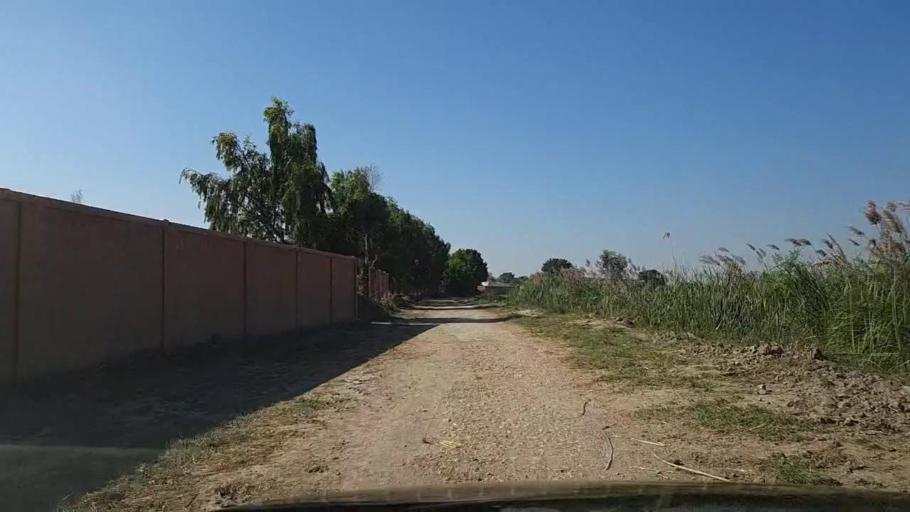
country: PK
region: Sindh
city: Thatta
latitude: 24.7033
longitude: 67.9073
